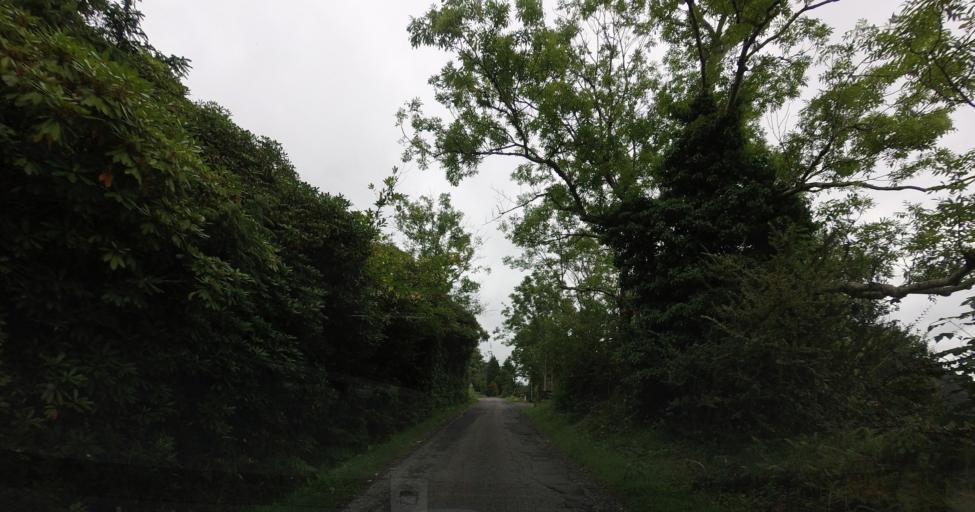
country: GB
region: Scotland
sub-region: Highland
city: Fort William
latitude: 57.2786
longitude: -5.5123
